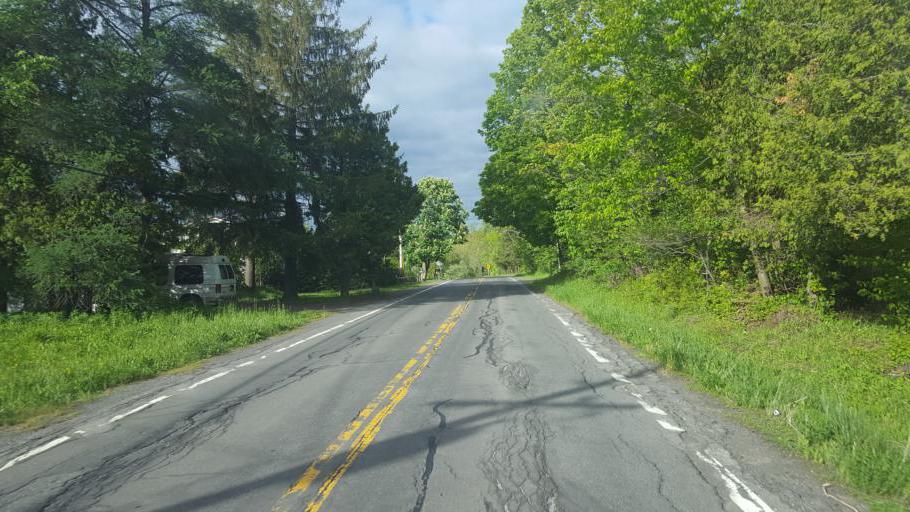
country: US
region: New York
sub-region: Otsego County
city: Richfield Springs
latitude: 42.9173
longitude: -74.9342
